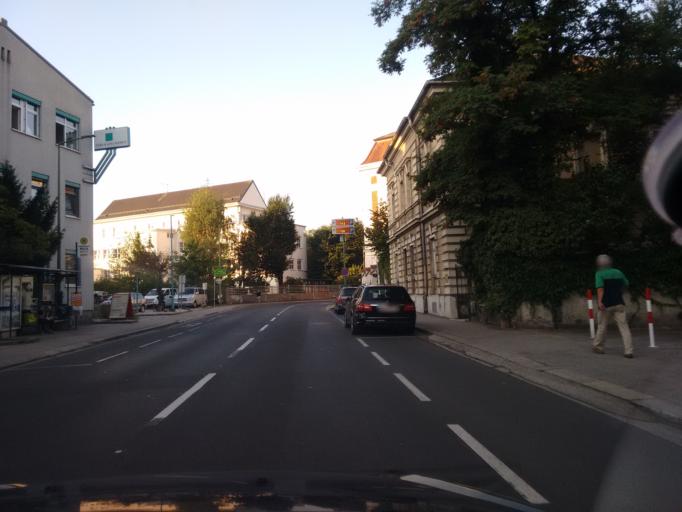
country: AT
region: Upper Austria
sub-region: Wels Stadt
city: Wels
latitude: 48.1625
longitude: 14.0311
